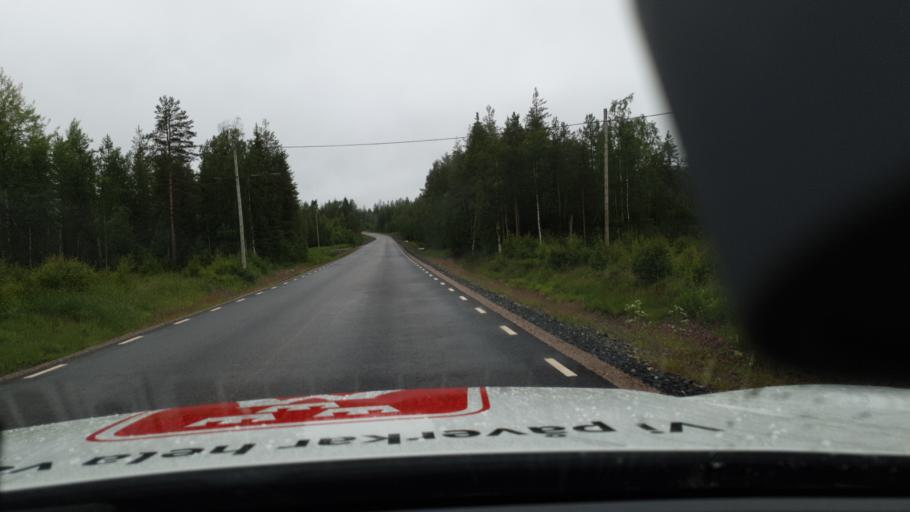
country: SE
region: Norrbotten
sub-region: Overtornea Kommun
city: OEvertornea
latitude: 66.5753
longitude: 23.3313
